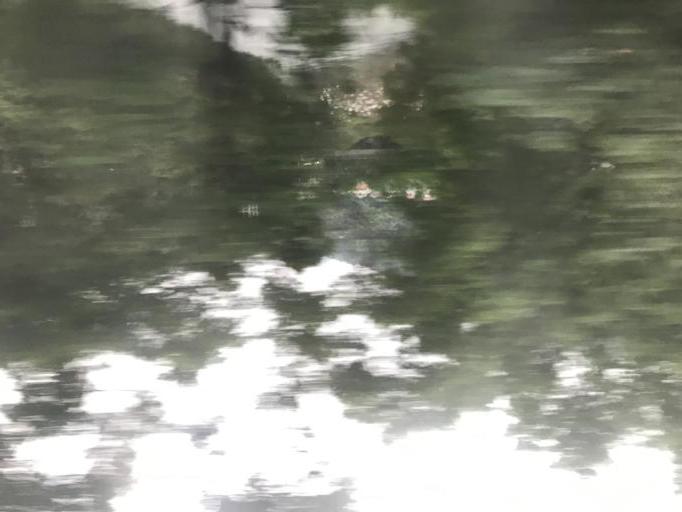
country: HK
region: Tai Po
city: Tai Po
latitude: 22.4381
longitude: 114.1883
